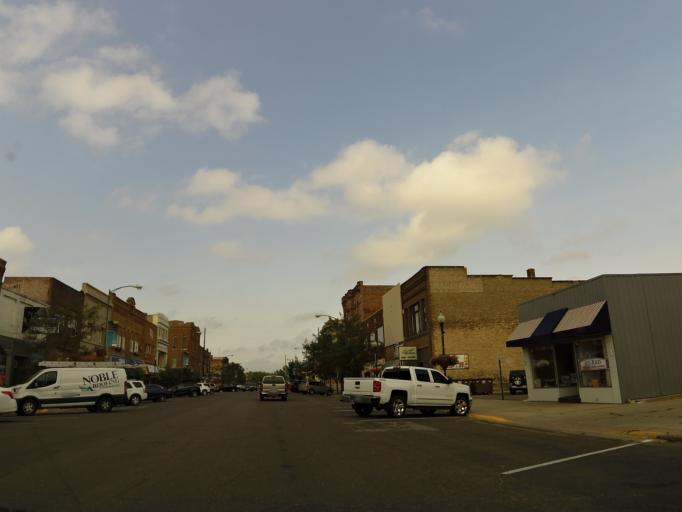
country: US
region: South Dakota
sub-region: Codington County
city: Watertown
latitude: 44.8996
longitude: -97.1149
